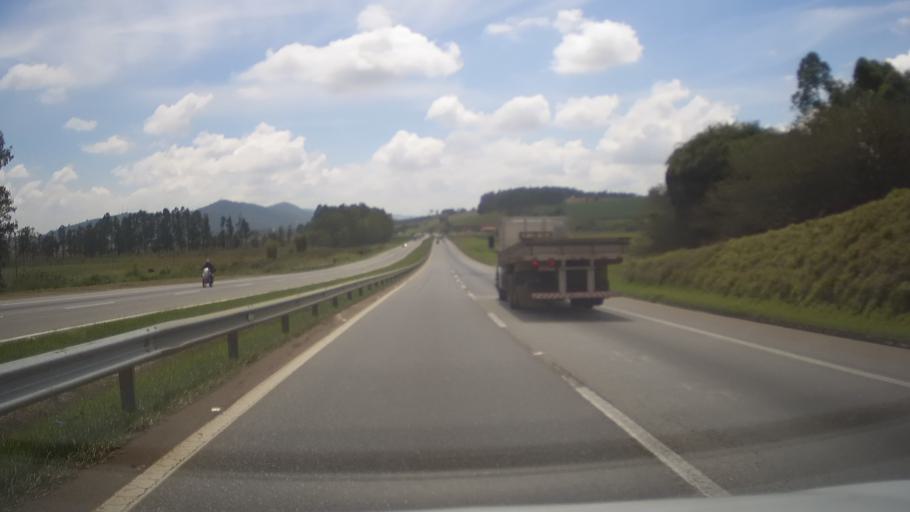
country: BR
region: Minas Gerais
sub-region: Santa Rita Do Sapucai
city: Santa Rita do Sapucai
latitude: -22.0985
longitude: -45.7191
